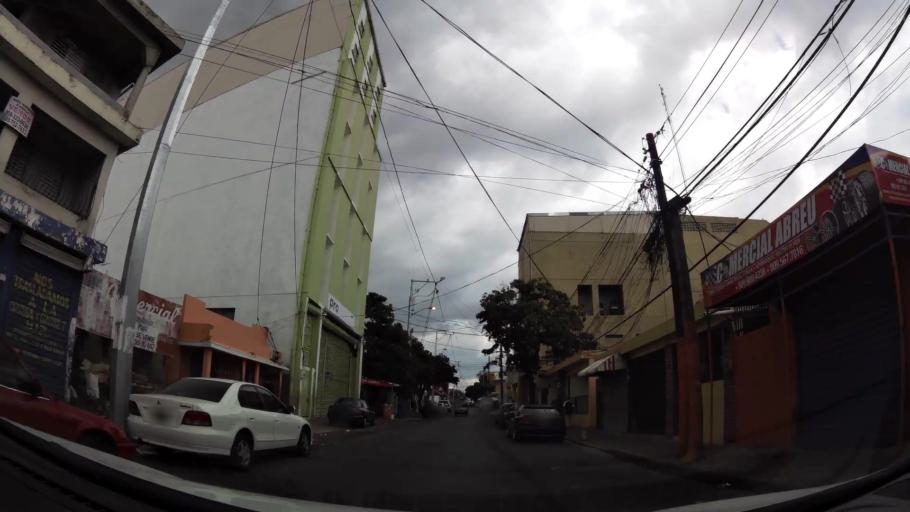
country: DO
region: Nacional
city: San Carlos
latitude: 18.4853
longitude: -69.9119
